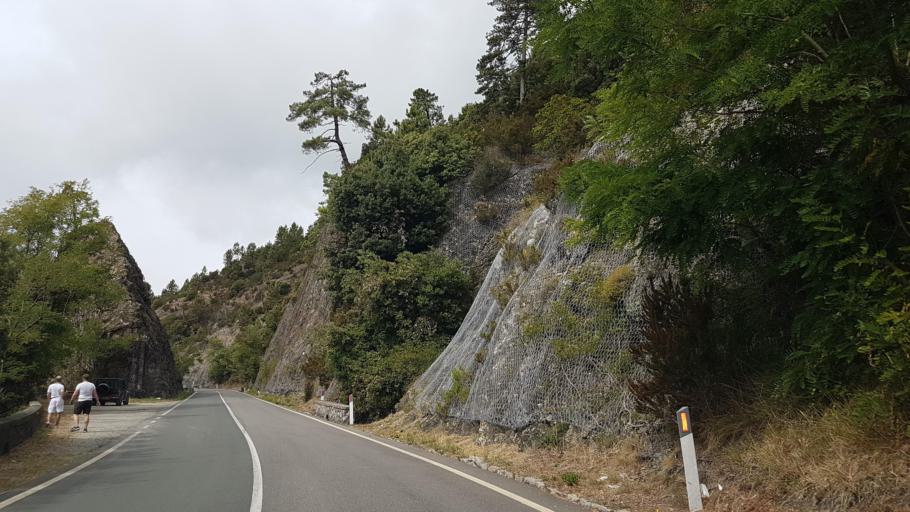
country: IT
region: Liguria
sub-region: Provincia di La Spezia
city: Framura
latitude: 44.2490
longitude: 9.5709
